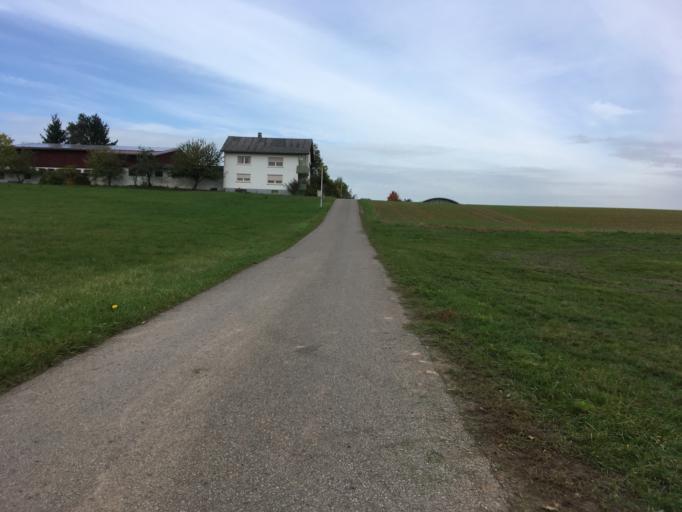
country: DE
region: Baden-Wuerttemberg
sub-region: Karlsruhe Region
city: Buchen
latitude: 49.5130
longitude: 9.3241
